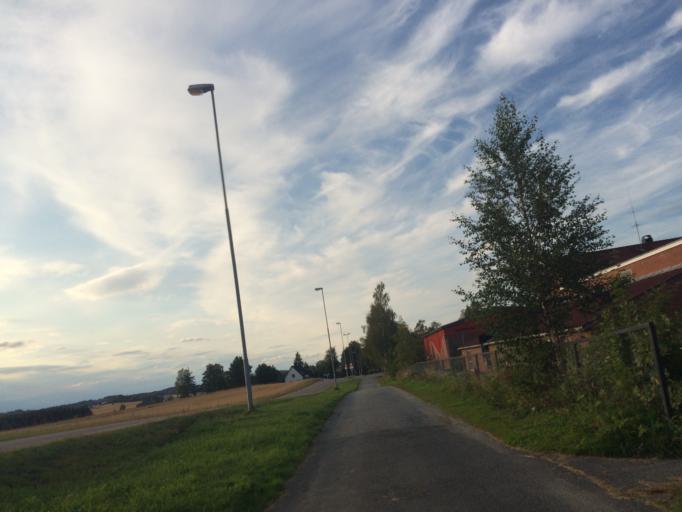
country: NO
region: Akershus
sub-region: Ski
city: Ski
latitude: 59.6773
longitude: 10.8850
